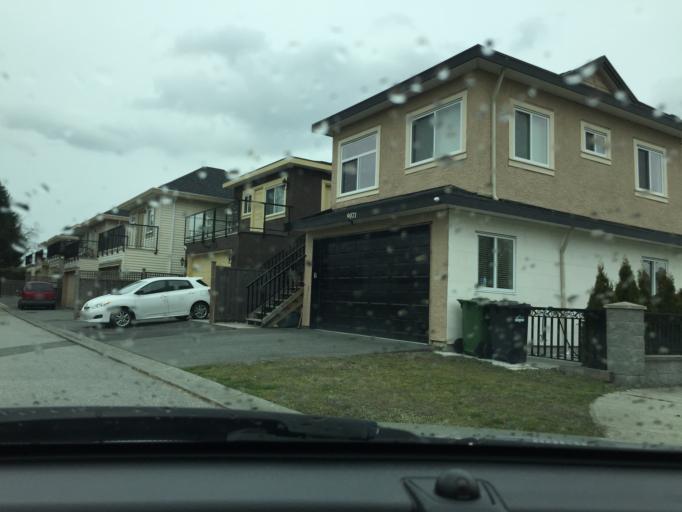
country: CA
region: British Columbia
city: Richmond
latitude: 49.1478
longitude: -123.1291
